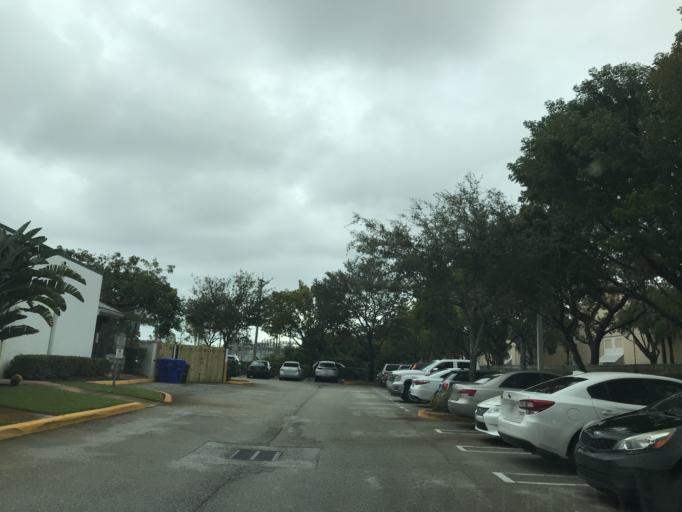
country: US
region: Florida
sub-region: Palm Beach County
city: Delray Beach
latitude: 26.4712
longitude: -80.0906
